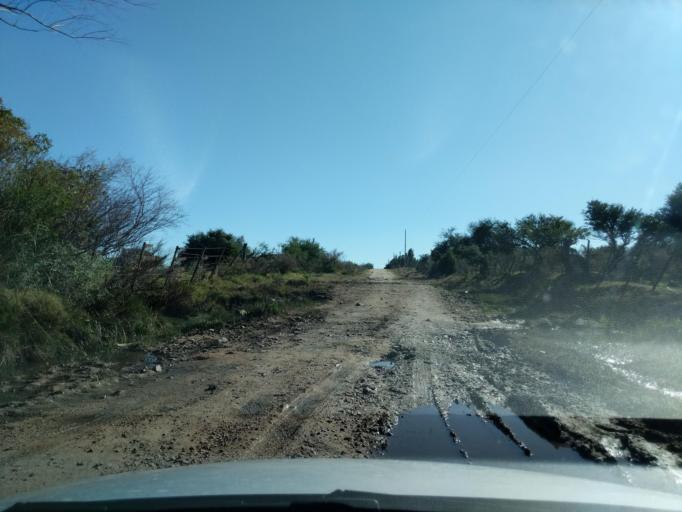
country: UY
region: Florida
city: Florida
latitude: -34.0784
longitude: -56.2680
